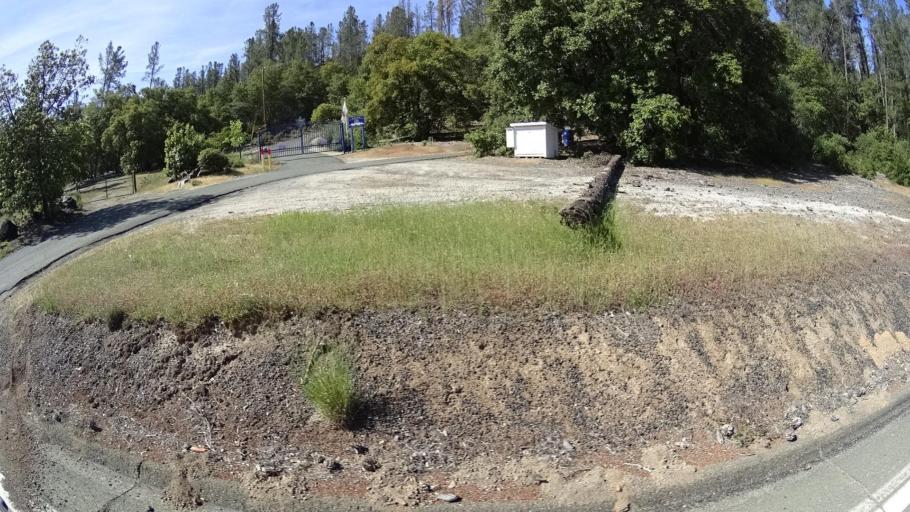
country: US
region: California
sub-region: Lake County
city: Kelseyville
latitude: 38.9161
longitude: -122.8018
